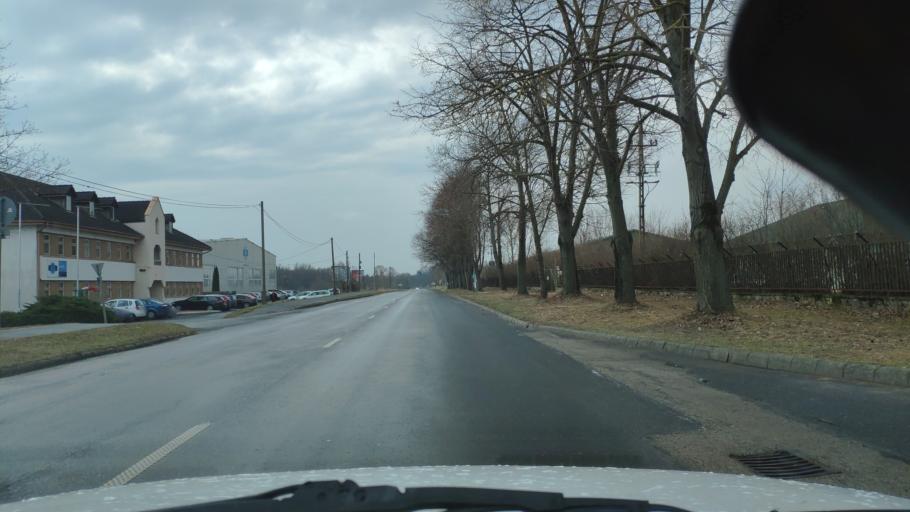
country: HU
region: Zala
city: Nagykanizsa
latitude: 46.4239
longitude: 16.9860
